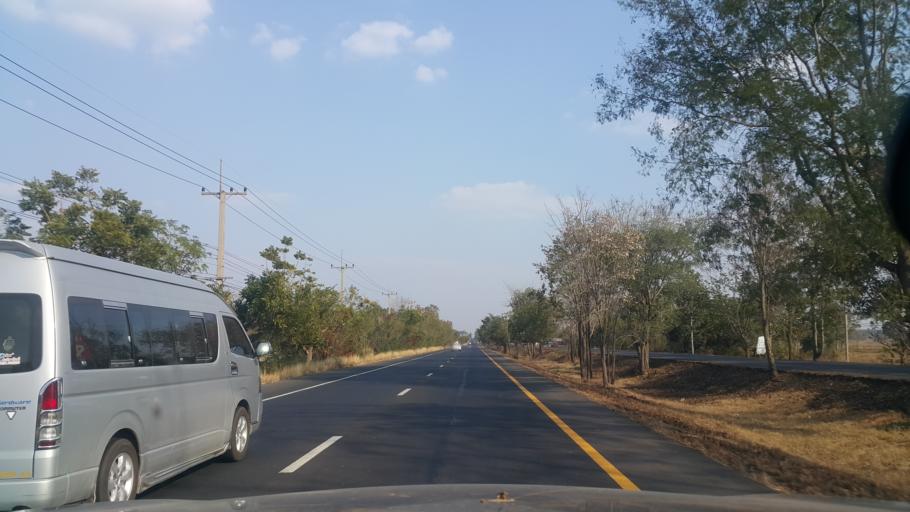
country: TH
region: Buriram
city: Non Suwan
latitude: 14.6529
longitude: 102.6501
